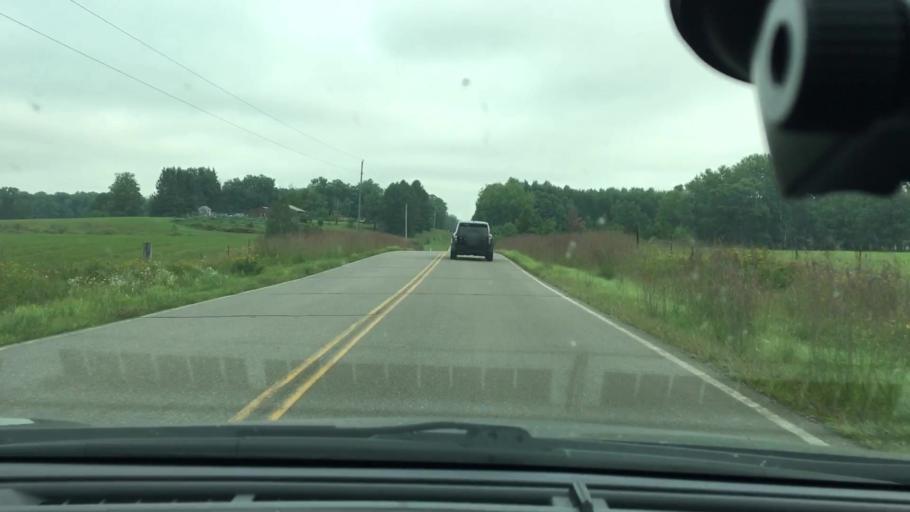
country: US
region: Minnesota
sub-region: Crow Wing County
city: Cross Lake
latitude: 46.6461
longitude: -94.0096
